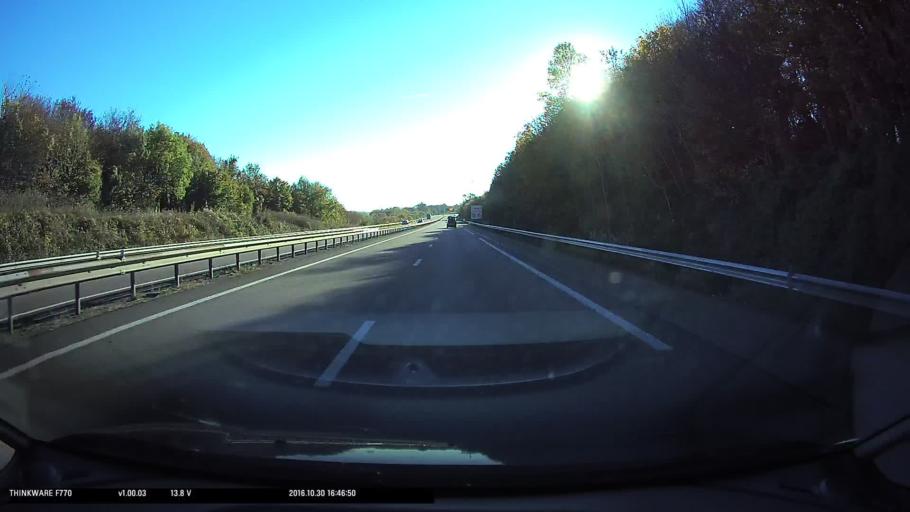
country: FR
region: Franche-Comte
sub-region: Departement du Doubs
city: Chatillon-le-Duc
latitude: 47.2936
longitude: 6.0179
